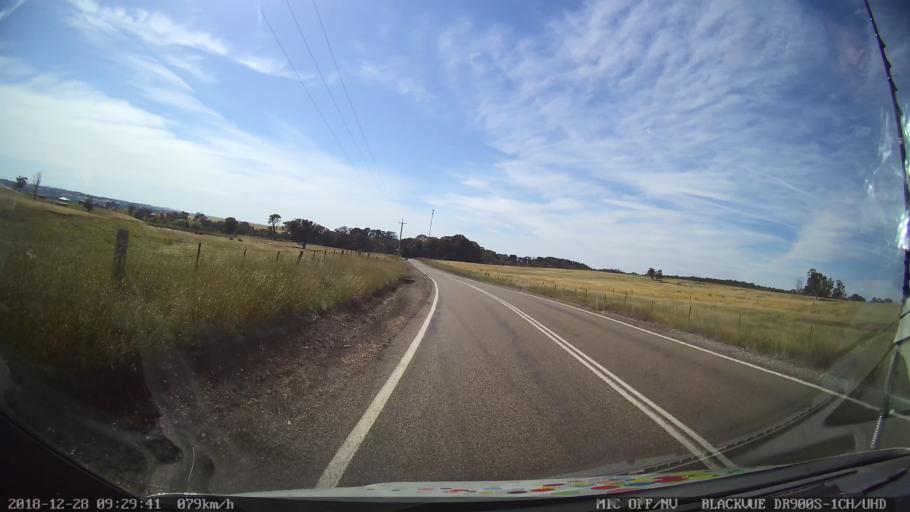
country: AU
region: New South Wales
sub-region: Upper Lachlan Shire
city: Crookwell
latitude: -34.4478
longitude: 149.4308
